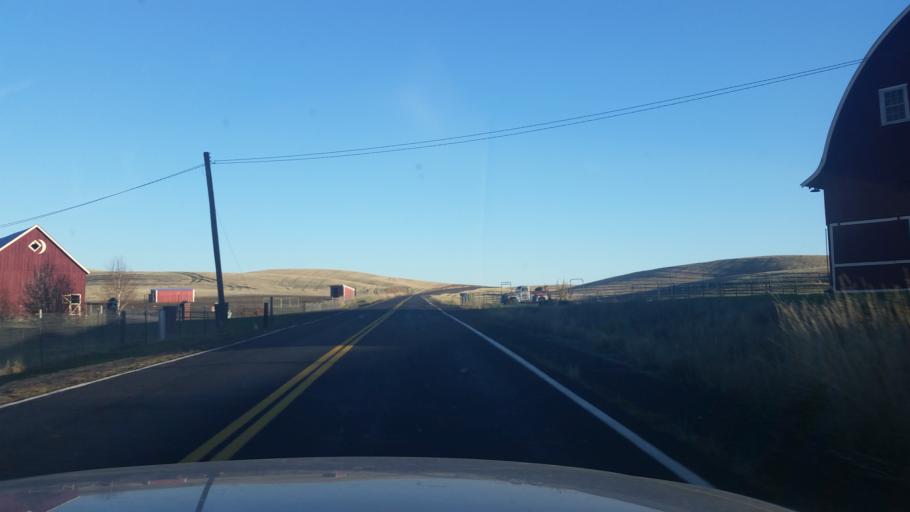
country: US
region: Washington
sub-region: Spokane County
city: Opportunity
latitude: 47.3755
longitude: -117.3046
